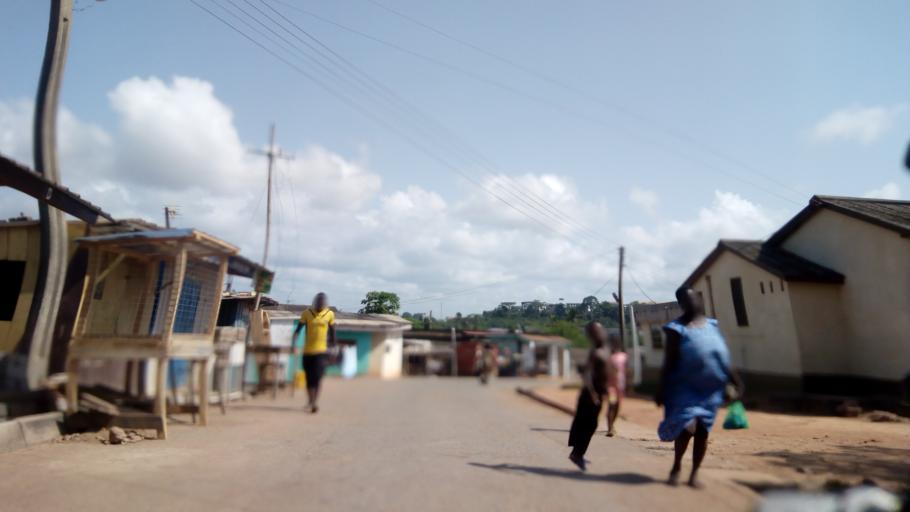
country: GH
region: Central
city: Cape Coast
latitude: 5.1137
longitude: -1.2665
